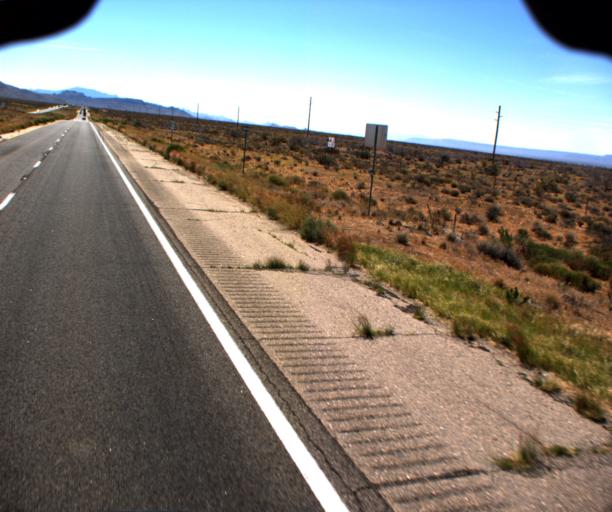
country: US
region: Arizona
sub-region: Mohave County
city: Golden Valley
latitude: 35.3096
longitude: -114.1964
